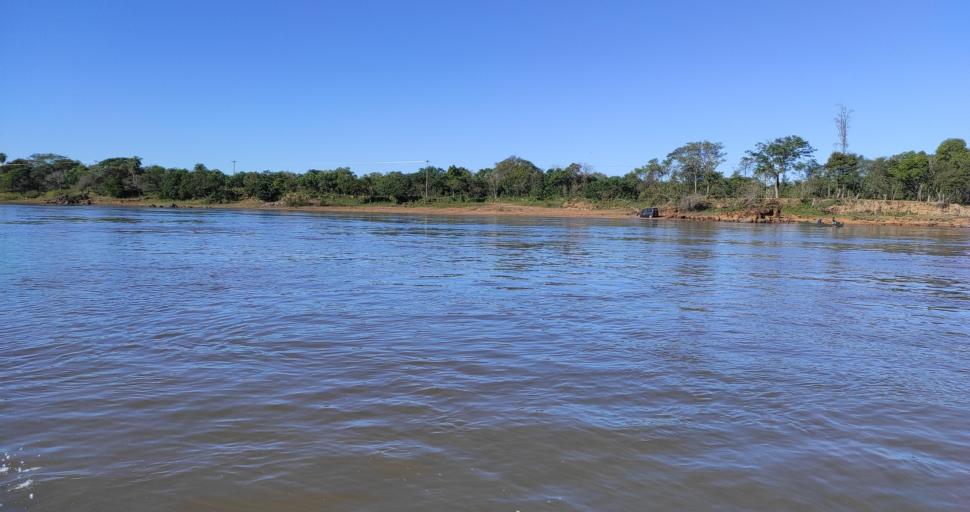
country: AR
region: Corrientes
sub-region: Departamento de Itati
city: Itati
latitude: -27.2633
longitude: -58.2602
